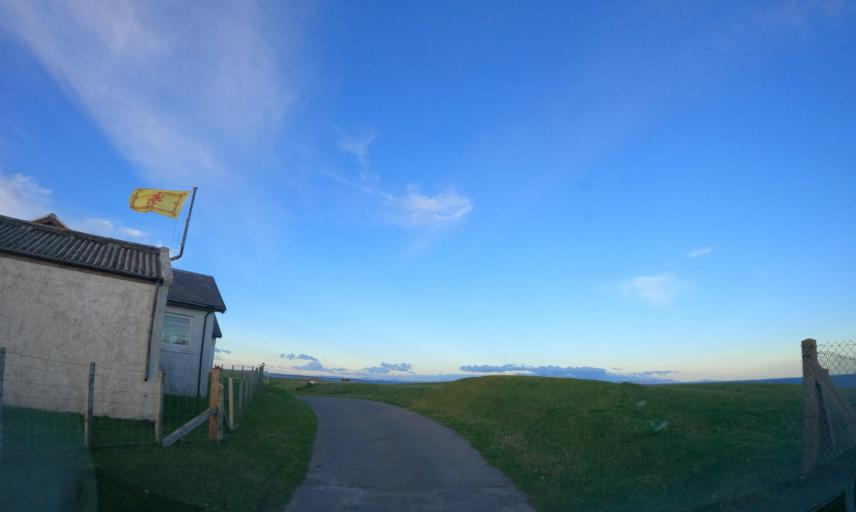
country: GB
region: Scotland
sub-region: Eilean Siar
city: Barra
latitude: 56.5002
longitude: -6.8071
